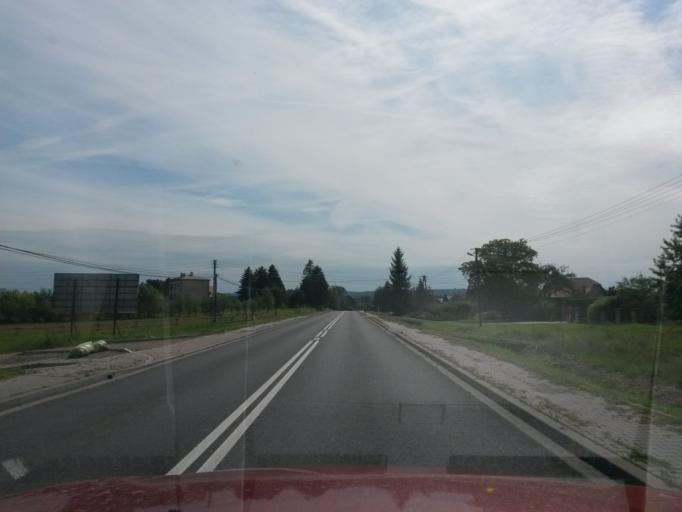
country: PL
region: Lesser Poland Voivodeship
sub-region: Powiat wielicki
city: Targowisko
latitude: 49.9794
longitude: 20.2928
